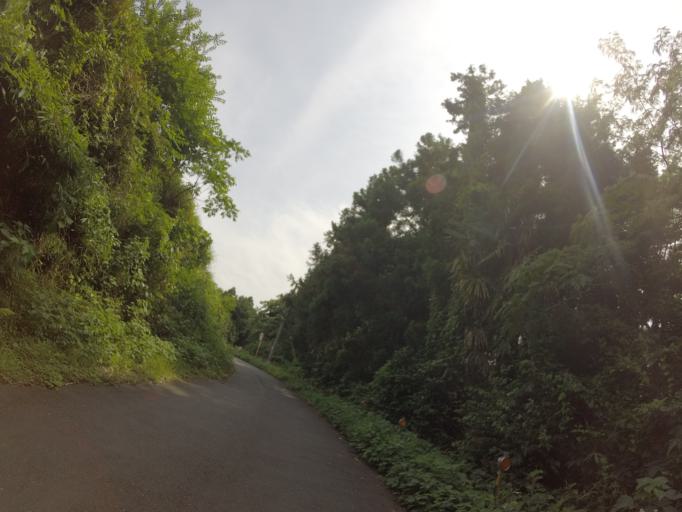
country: JP
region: Shizuoka
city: Fujinomiya
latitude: 35.2787
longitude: 138.5696
